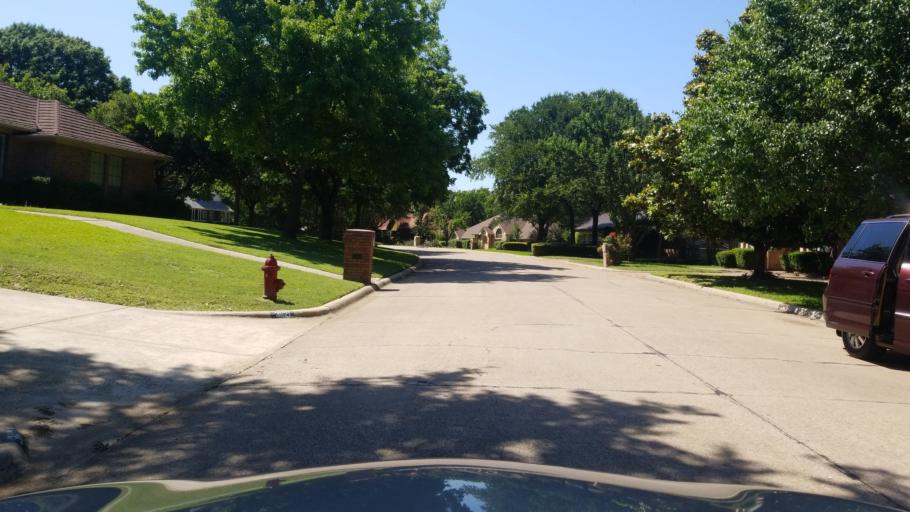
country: US
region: Texas
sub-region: Dallas County
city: Grand Prairie
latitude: 32.6866
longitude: -96.9962
